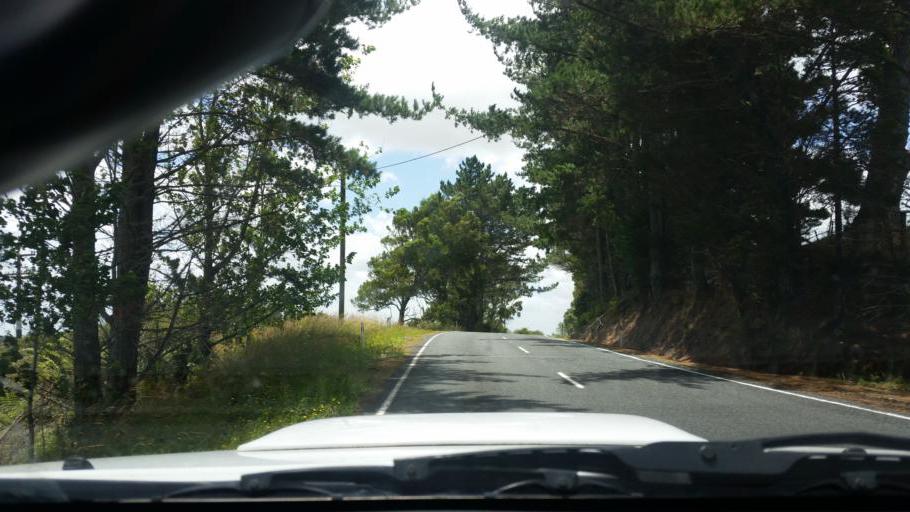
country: NZ
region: Northland
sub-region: Whangarei
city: Ruakaka
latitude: -36.0692
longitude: 174.2656
